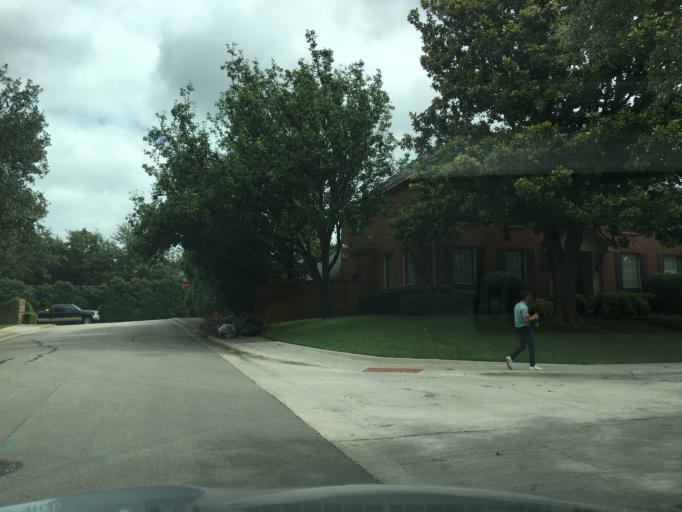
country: US
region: Texas
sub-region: Dallas County
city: University Park
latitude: 32.8798
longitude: -96.7431
